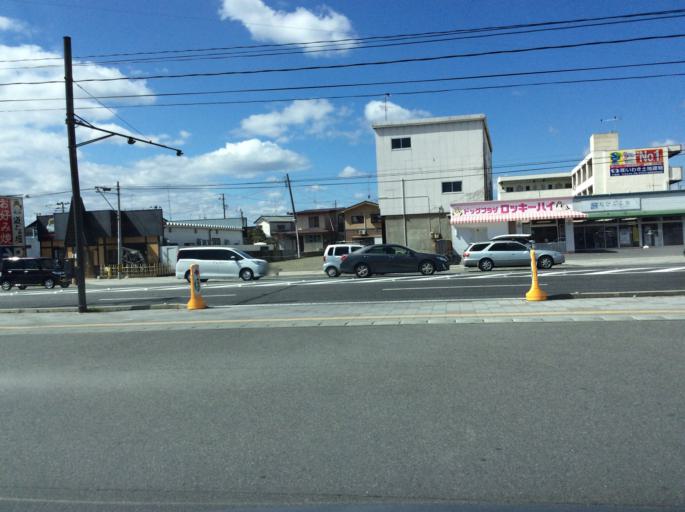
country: JP
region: Fukushima
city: Iwaki
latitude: 36.9572
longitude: 140.9039
